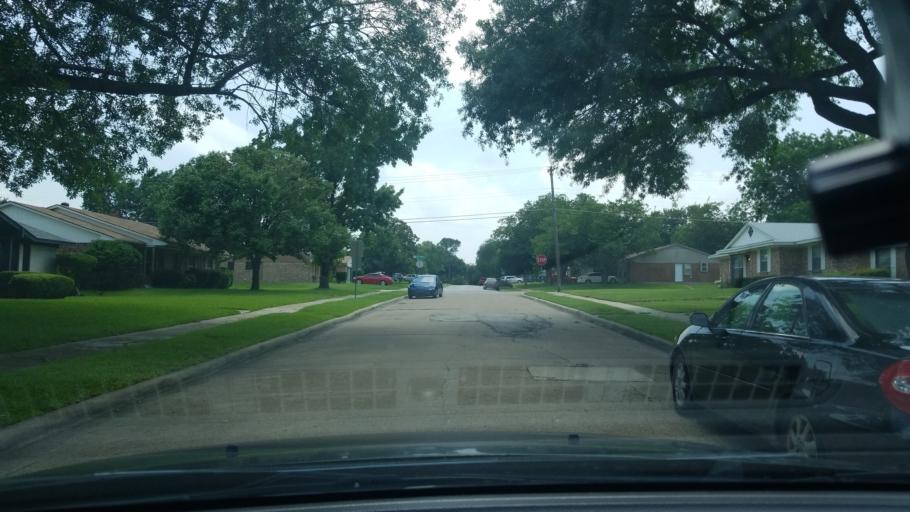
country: US
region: Texas
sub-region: Dallas County
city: Mesquite
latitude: 32.8028
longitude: -96.6385
